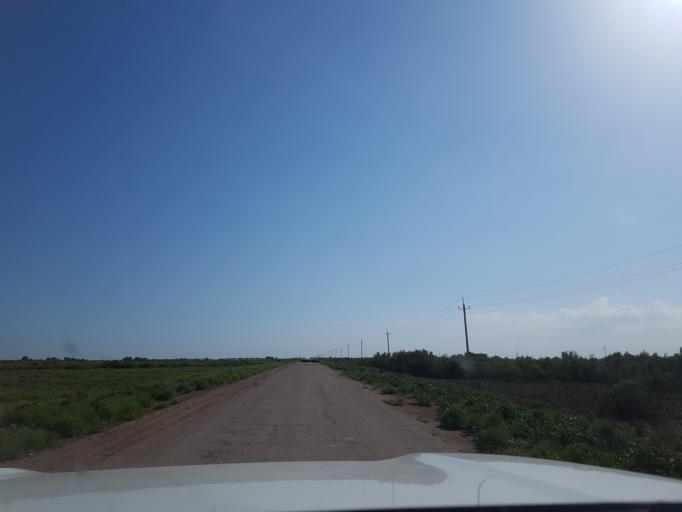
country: TM
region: Dasoguz
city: Koeneuergench
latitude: 42.0559
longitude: 58.8383
